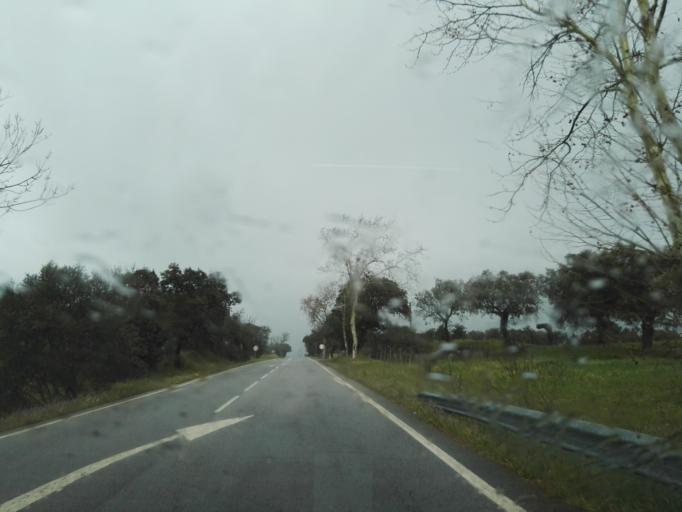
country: PT
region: Portalegre
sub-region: Arronches
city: Arronches
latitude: 39.0973
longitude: -7.2806
